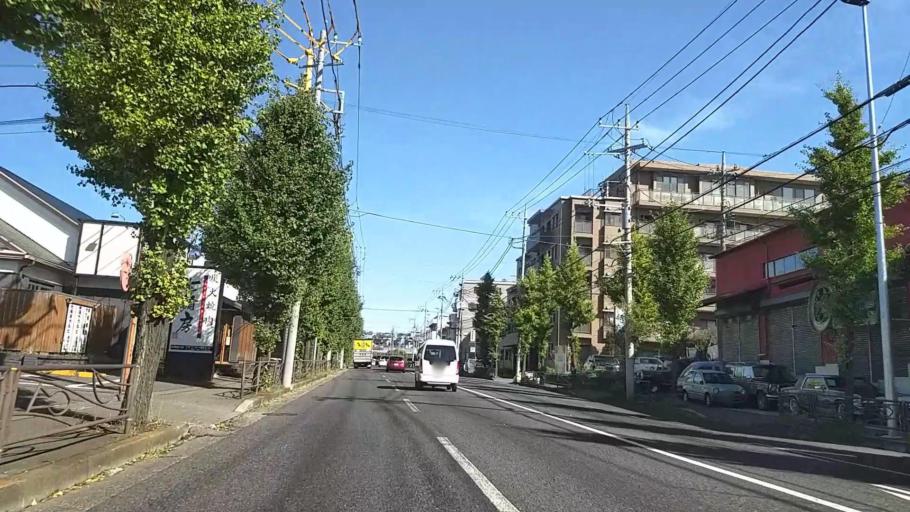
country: JP
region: Tokyo
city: Chofugaoka
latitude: 35.5763
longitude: 139.6118
